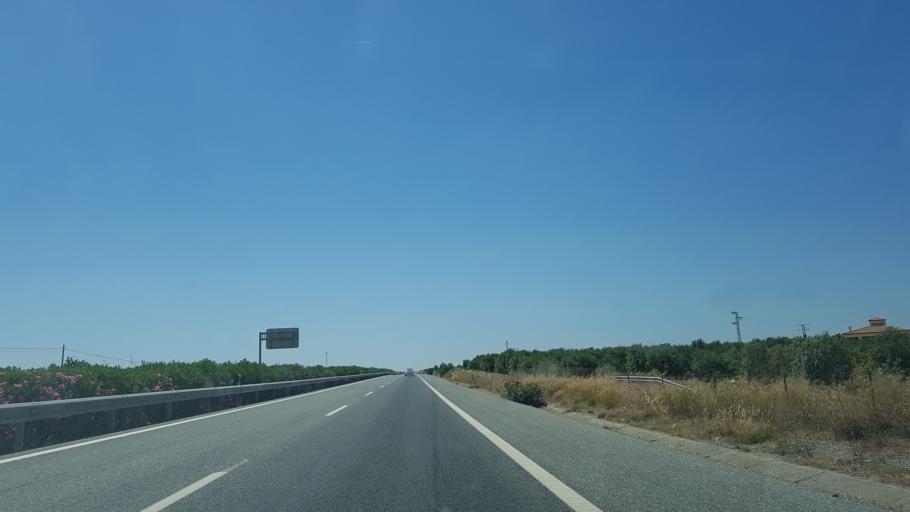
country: ES
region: Andalusia
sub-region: Provincia de Sevilla
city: La Puebla de Cazalla
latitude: 37.2268
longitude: -5.3365
